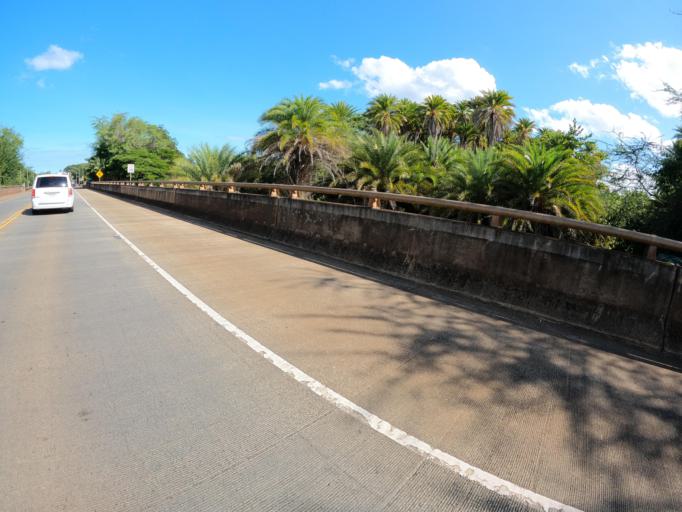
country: US
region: Hawaii
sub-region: Honolulu County
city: Hale'iwa
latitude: 21.5993
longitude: -158.0997
